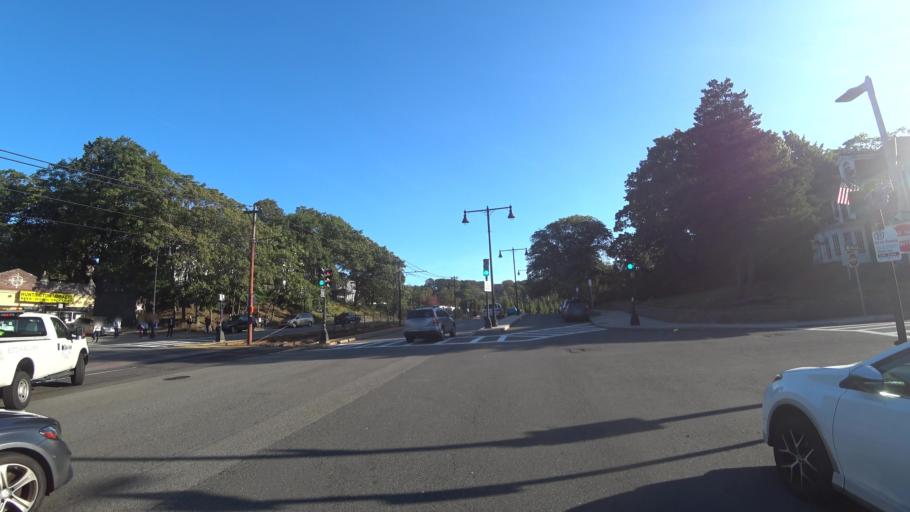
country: US
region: Massachusetts
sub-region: Norfolk County
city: Brookline
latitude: 42.3402
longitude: -71.1513
